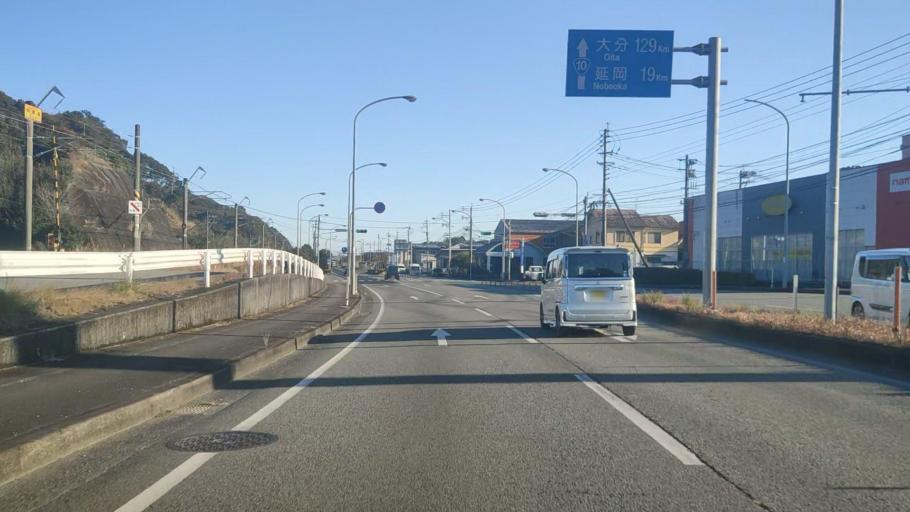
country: JP
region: Miyazaki
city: Nobeoka
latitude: 32.4500
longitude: 131.6394
